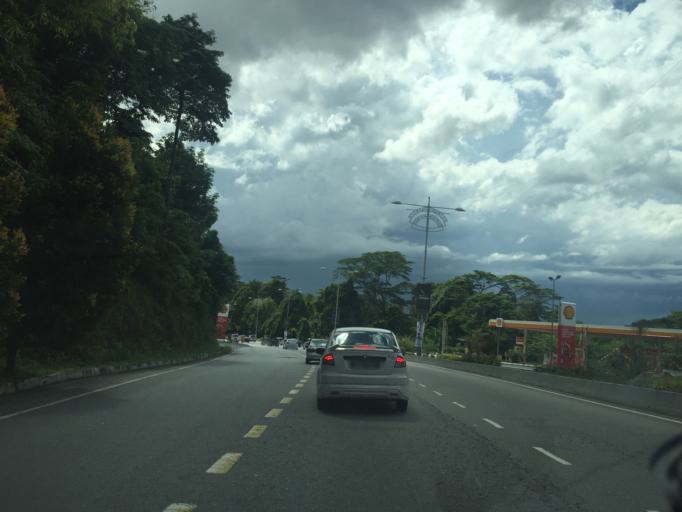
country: MY
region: Negeri Sembilan
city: Seremban
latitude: 2.7233
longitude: 101.9250
